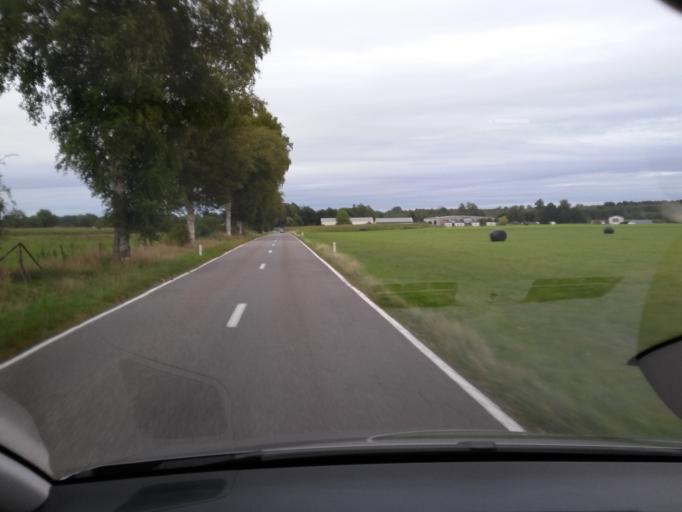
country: BE
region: Wallonia
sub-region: Province du Luxembourg
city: Etalle
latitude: 49.6705
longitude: 5.5718
